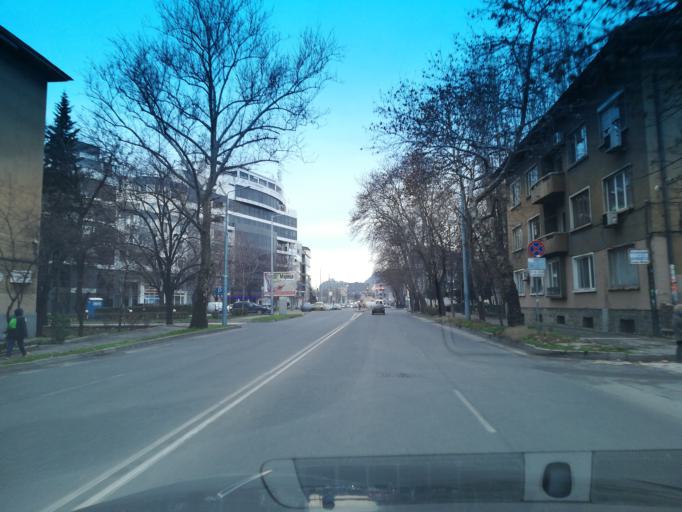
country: BG
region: Plovdiv
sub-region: Obshtina Plovdiv
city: Plovdiv
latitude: 42.1363
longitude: 24.7557
